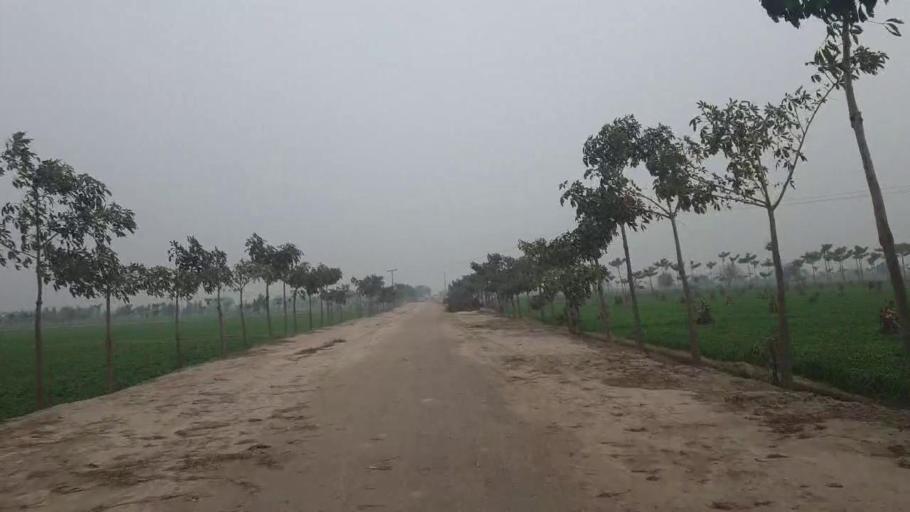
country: PK
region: Sindh
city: Tando Adam
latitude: 25.7474
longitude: 68.6754
